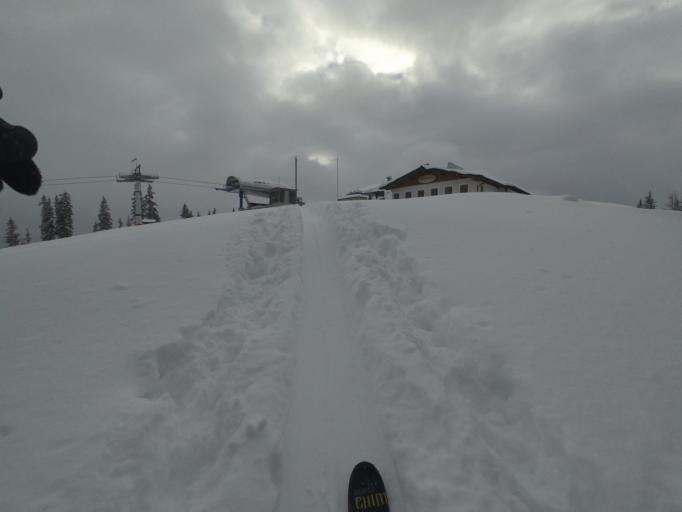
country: AT
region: Salzburg
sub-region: Politischer Bezirk Sankt Johann im Pongau
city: Wagrain
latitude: 47.3105
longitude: 13.2734
